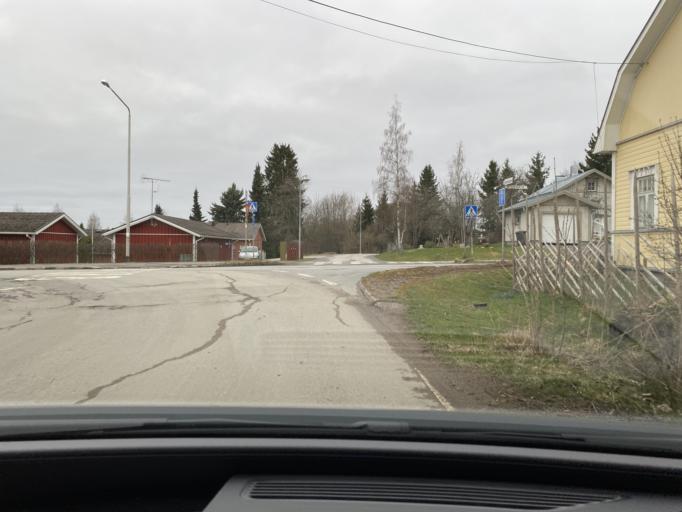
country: FI
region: Satakunta
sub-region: Pori
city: Huittinen
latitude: 61.1912
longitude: 22.7000
